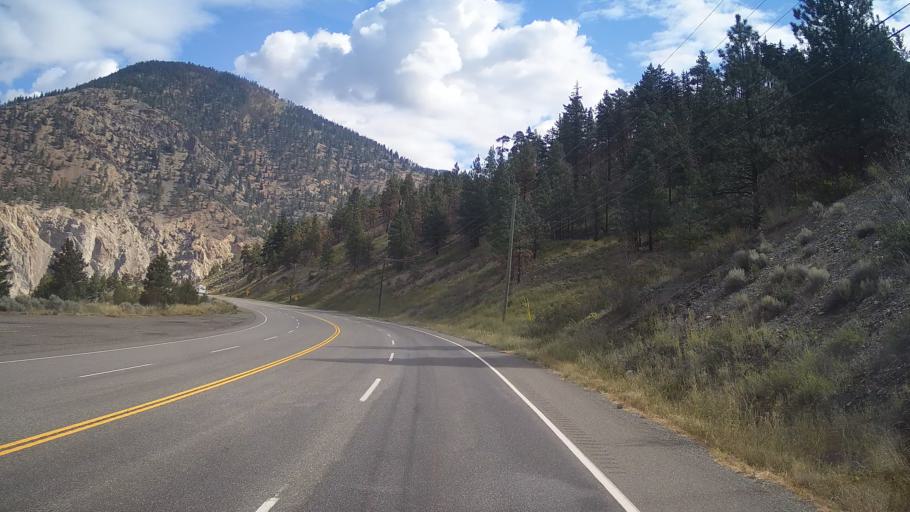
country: CA
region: British Columbia
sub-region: Thompson-Nicola Regional District
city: Ashcroft
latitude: 50.2553
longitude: -121.5440
